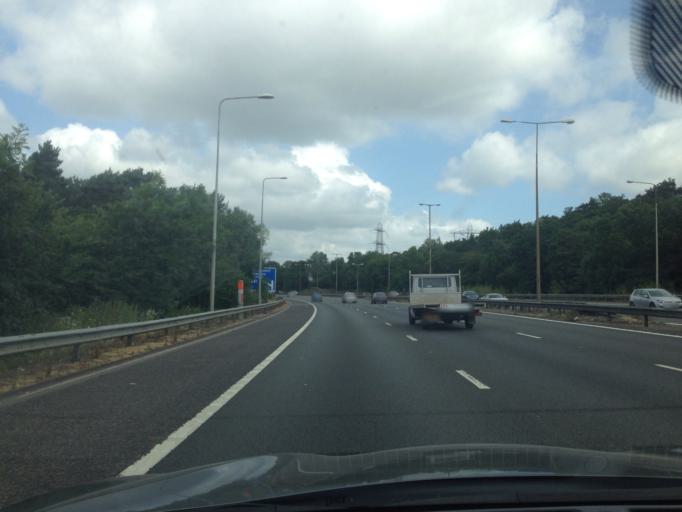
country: GB
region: England
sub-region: Hertfordshire
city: Bushey
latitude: 51.6572
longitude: -0.3447
